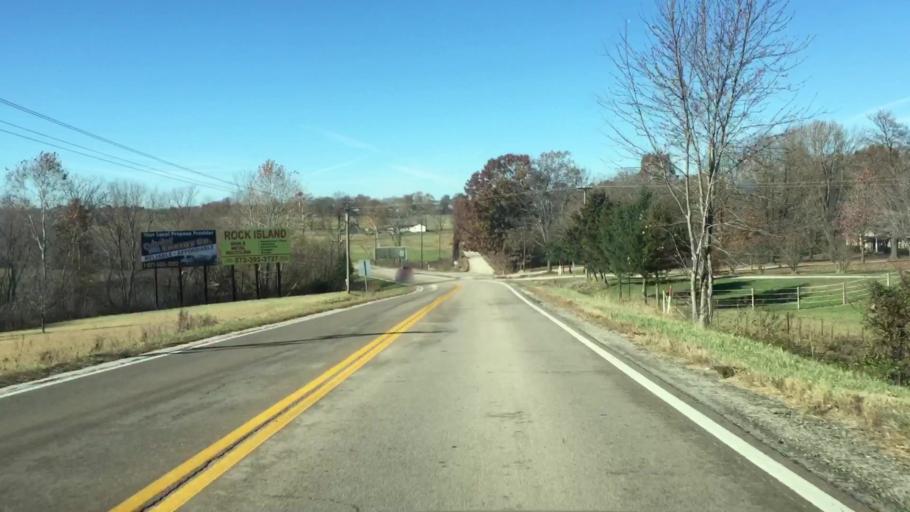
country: US
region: Missouri
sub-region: Miller County
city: Eldon
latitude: 38.3643
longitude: -92.5546
